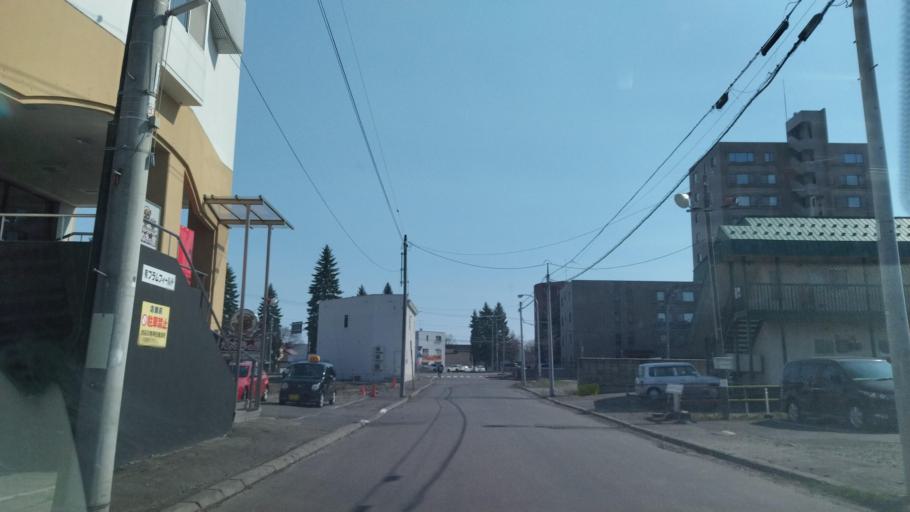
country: JP
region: Hokkaido
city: Obihiro
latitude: 42.9147
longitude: 143.1976
